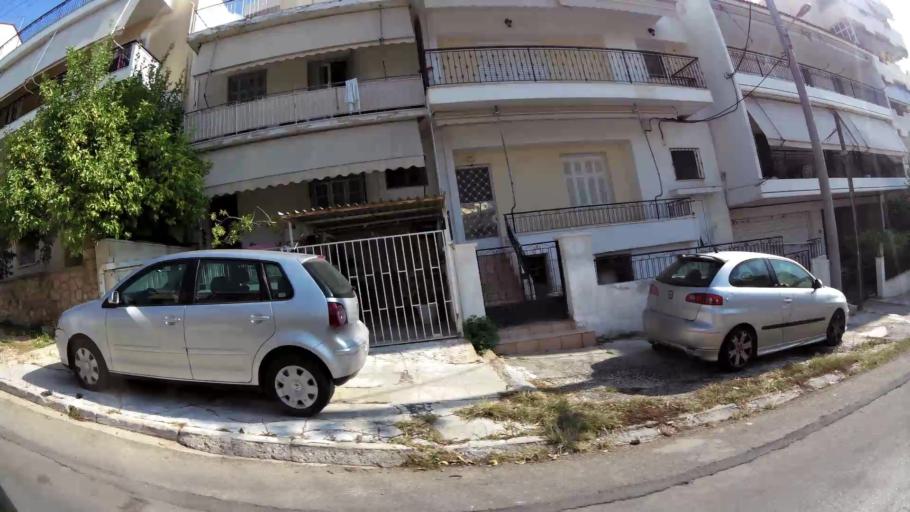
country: GR
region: Attica
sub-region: Nomarchia Athinas
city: Ilioupoli
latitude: 37.9216
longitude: 23.7573
